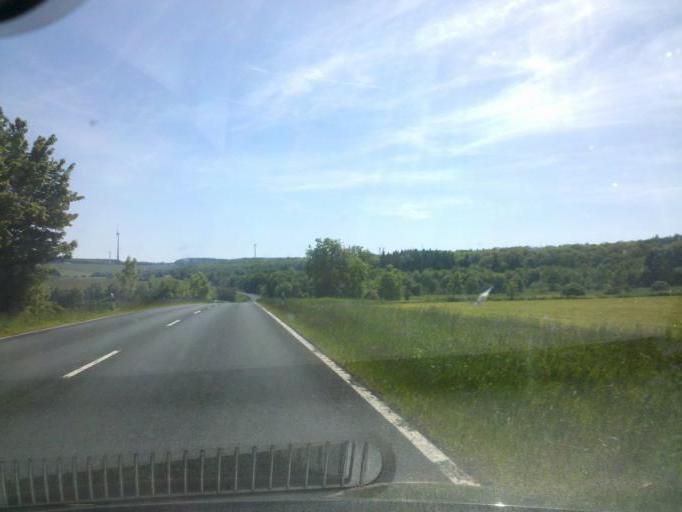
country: DE
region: Rheinland-Pfalz
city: Homberg
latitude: 50.6748
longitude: 8.1408
